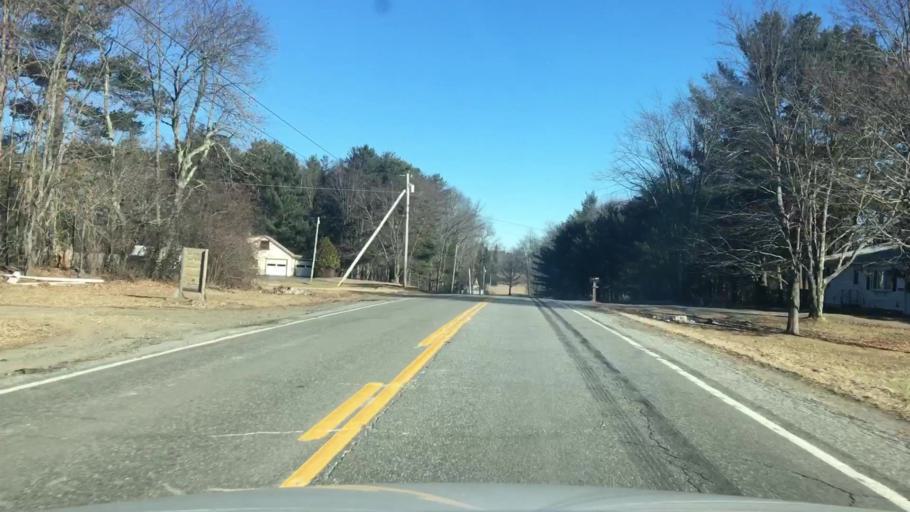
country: US
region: Maine
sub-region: Kennebec County
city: Benton
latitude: 44.5762
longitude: -69.5621
